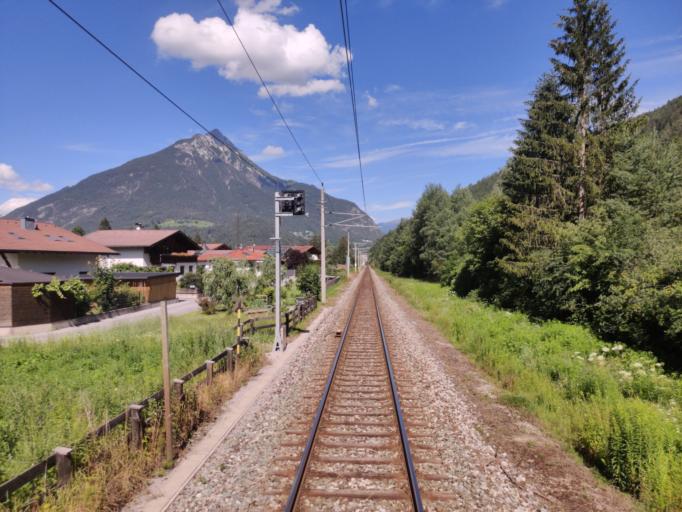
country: AT
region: Tyrol
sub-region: Politischer Bezirk Imst
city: Imsterberg
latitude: 47.2134
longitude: 10.7205
